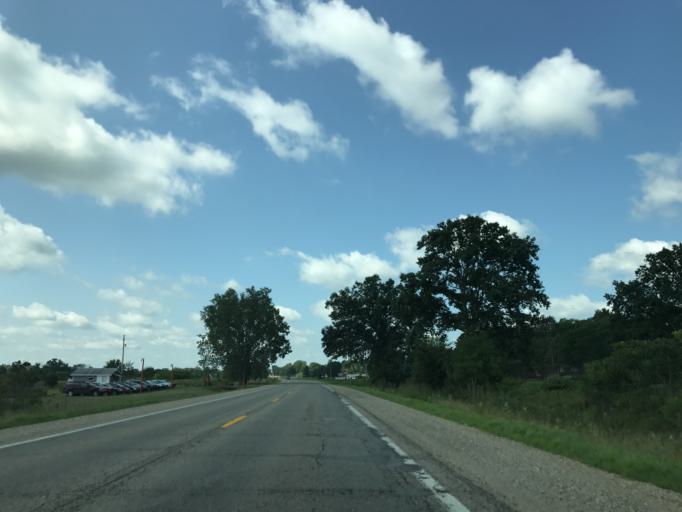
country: US
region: Michigan
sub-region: Branch County
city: Bronson
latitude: 41.8635
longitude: -85.2281
